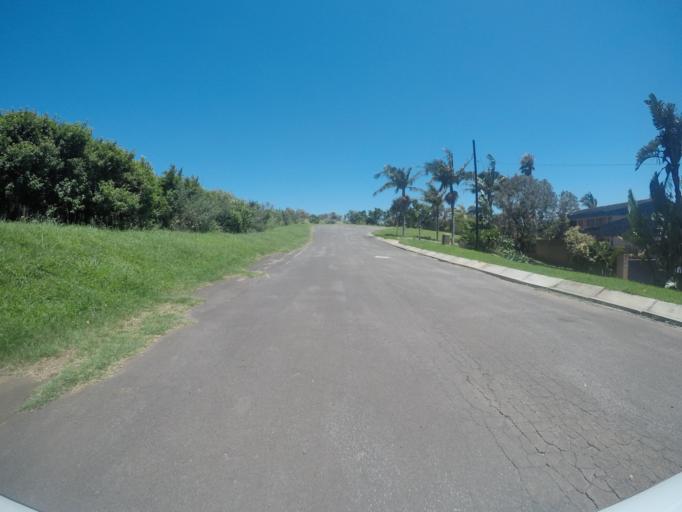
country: ZA
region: Eastern Cape
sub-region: Buffalo City Metropolitan Municipality
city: East London
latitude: -32.9334
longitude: 28.0041
